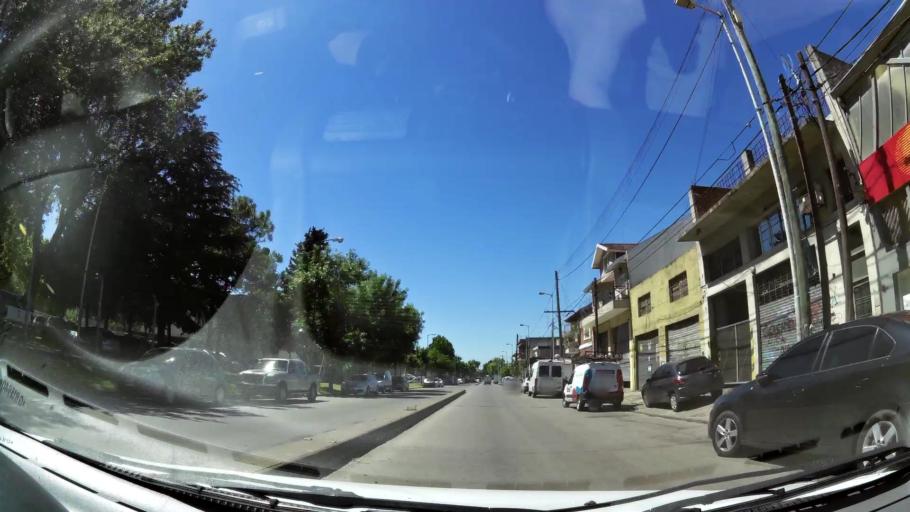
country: AR
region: Buenos Aires
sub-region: Partido de General San Martin
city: General San Martin
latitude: -34.5354
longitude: -58.5479
